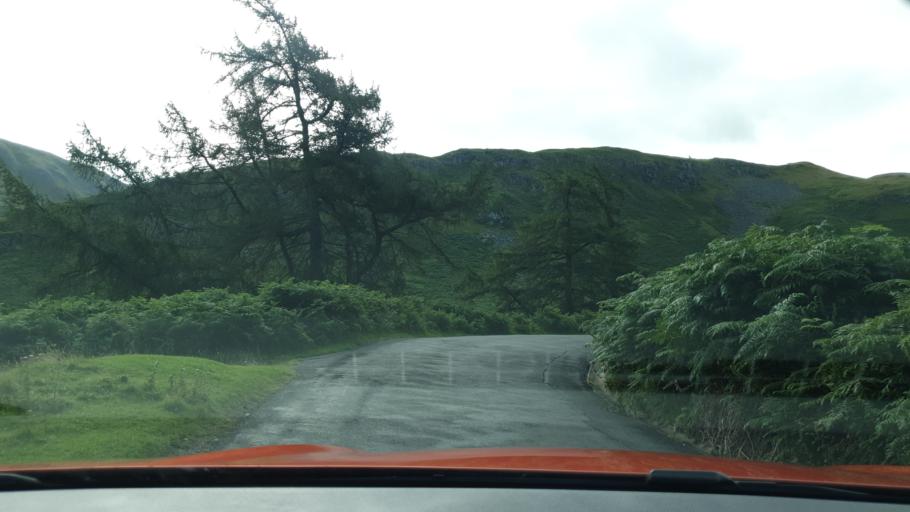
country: GB
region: England
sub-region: Cumbria
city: Penrith
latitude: 54.5670
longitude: -2.8689
